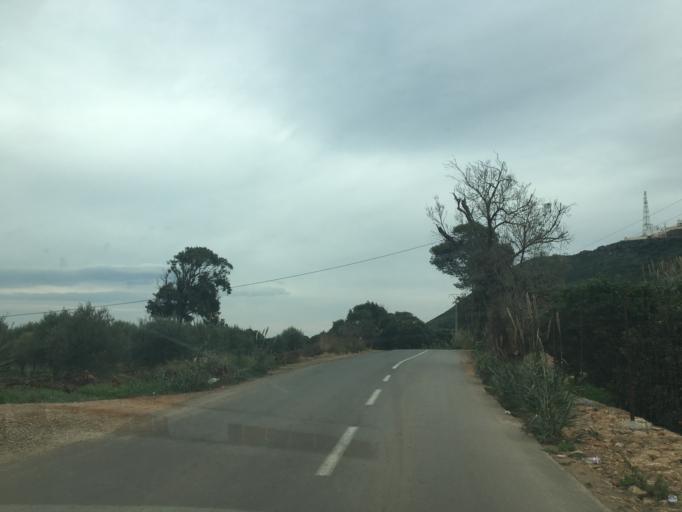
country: DZ
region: Tipaza
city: Tipasa
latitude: 36.6343
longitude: 2.3913
